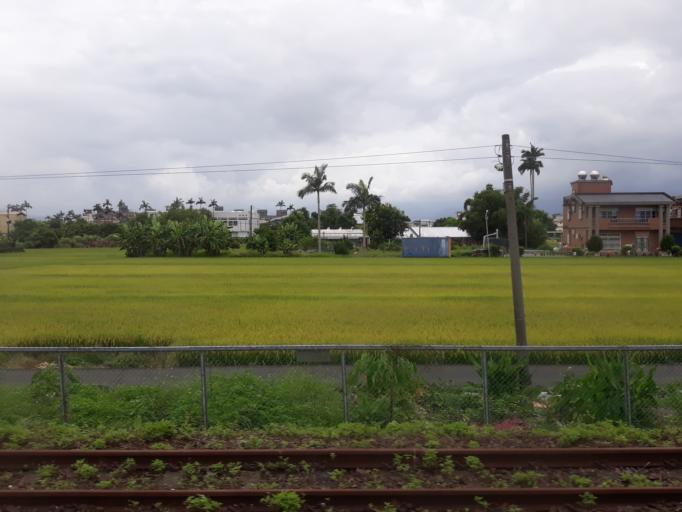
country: TW
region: Taiwan
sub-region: Yilan
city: Yilan
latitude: 24.7001
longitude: 121.7753
